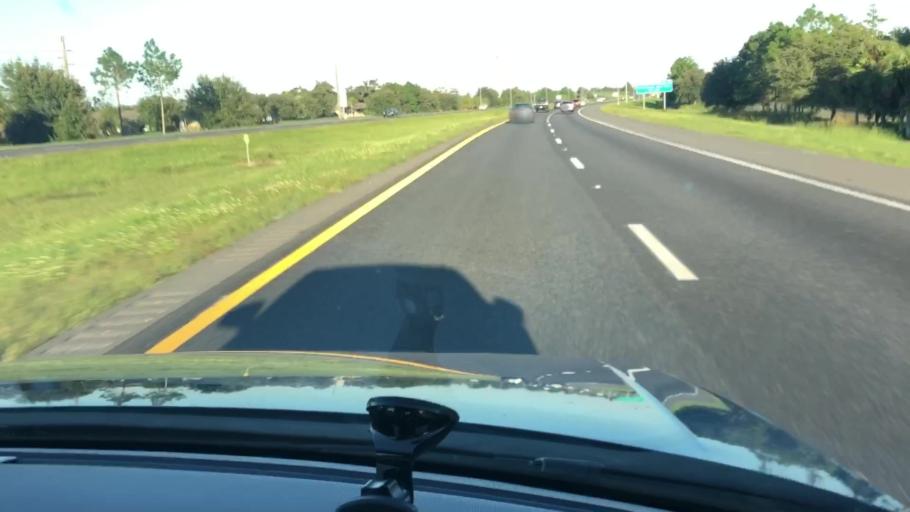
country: US
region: Florida
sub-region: Orange County
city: Winter Garden
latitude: 28.5146
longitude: -81.5991
